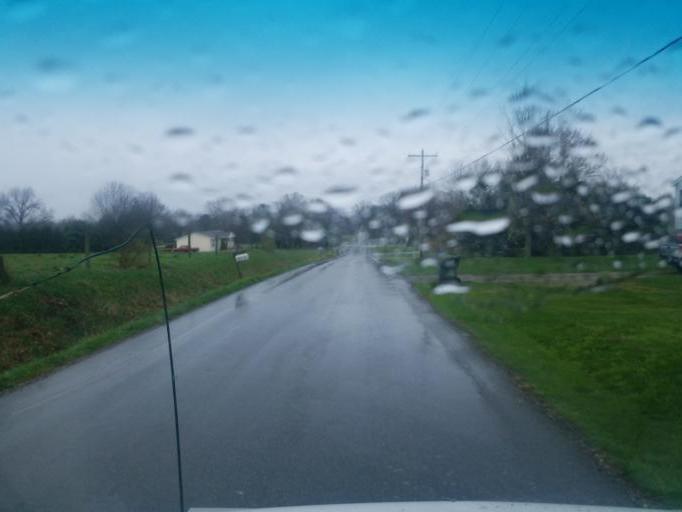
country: US
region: Ohio
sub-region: Wayne County
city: Wooster
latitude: 40.7332
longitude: -81.9360
